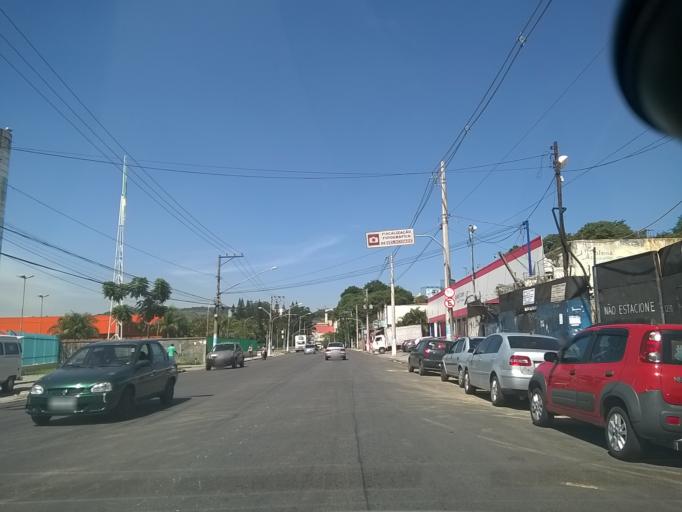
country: BR
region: Sao Paulo
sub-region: Caieiras
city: Caieiras
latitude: -23.4350
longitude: -46.7201
